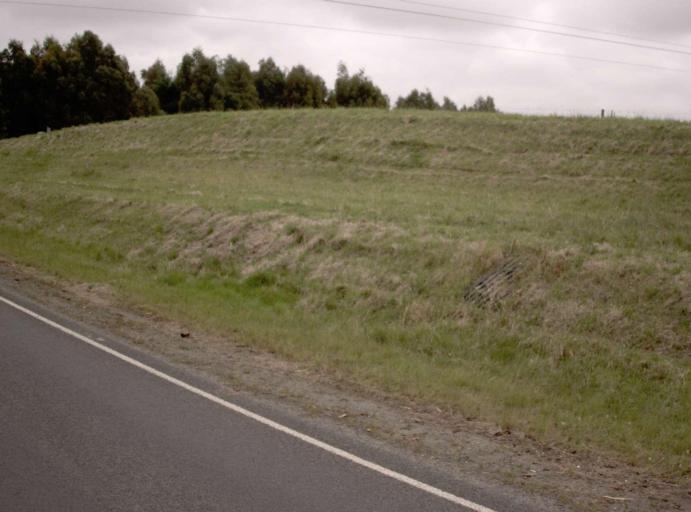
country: AU
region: Victoria
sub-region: Latrobe
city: Traralgon
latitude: -38.2496
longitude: 146.5444
